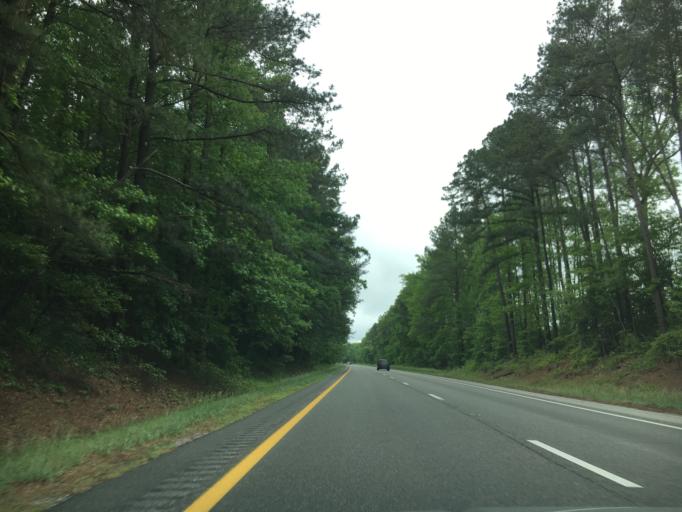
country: US
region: Virginia
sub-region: Brunswick County
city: Lawrenceville
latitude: 36.9055
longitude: -77.7882
